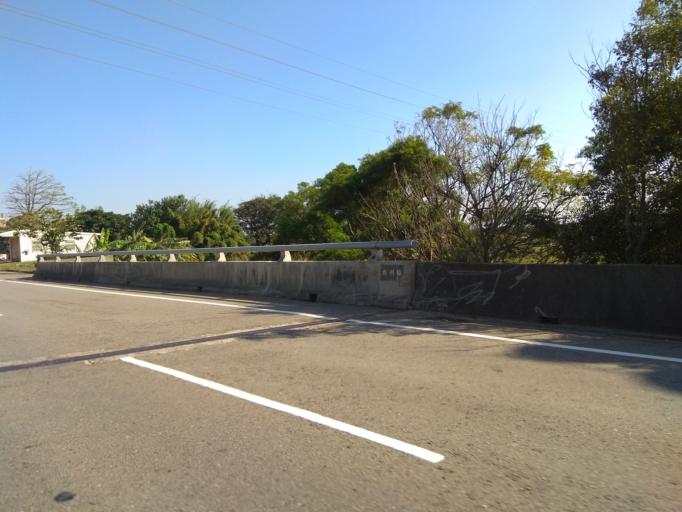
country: TW
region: Taiwan
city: Taoyuan City
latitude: 25.0370
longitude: 121.1250
